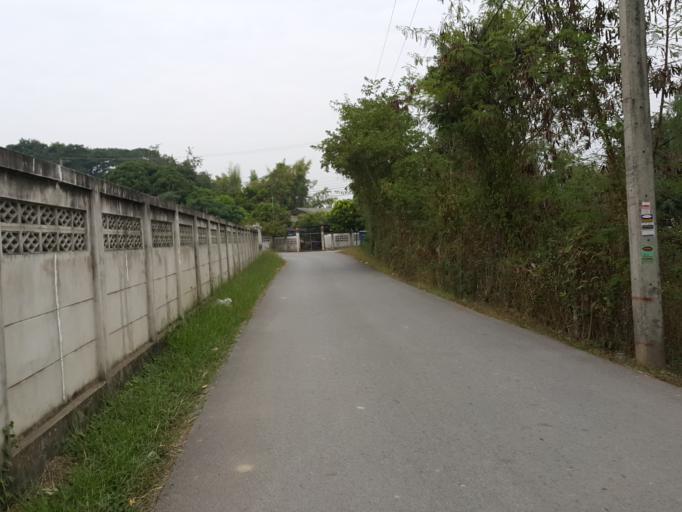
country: TH
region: Chiang Mai
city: San Kamphaeng
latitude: 18.7885
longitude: 99.1023
